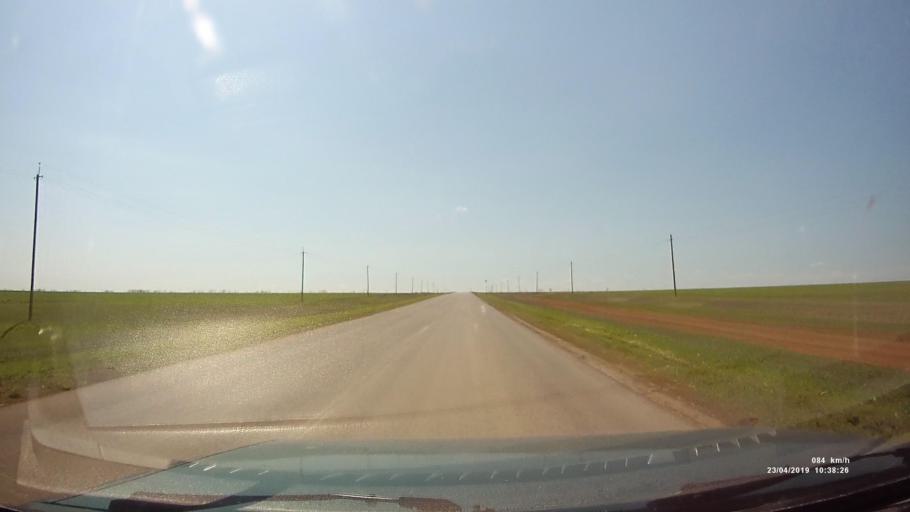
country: RU
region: Kalmykiya
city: Yashalta
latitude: 46.5325
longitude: 42.6388
